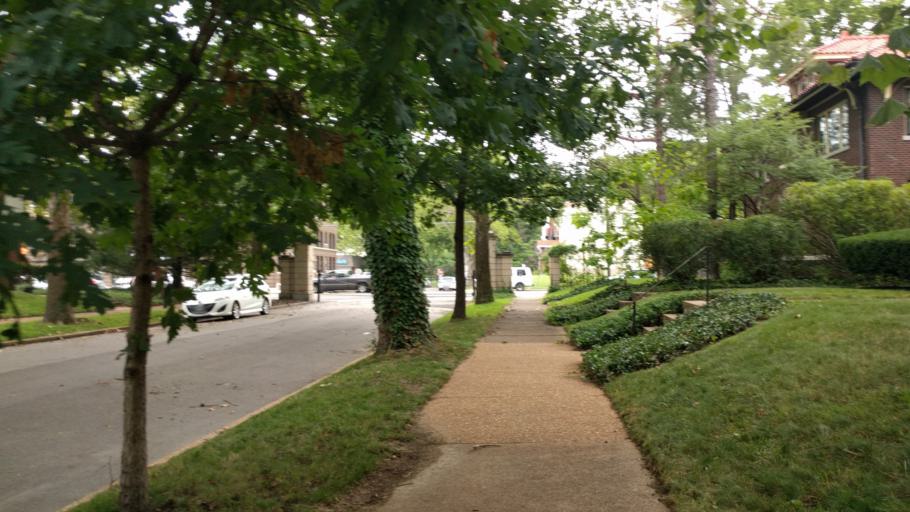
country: US
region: Missouri
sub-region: Saint Louis County
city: University City
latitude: 38.6523
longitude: -90.3142
